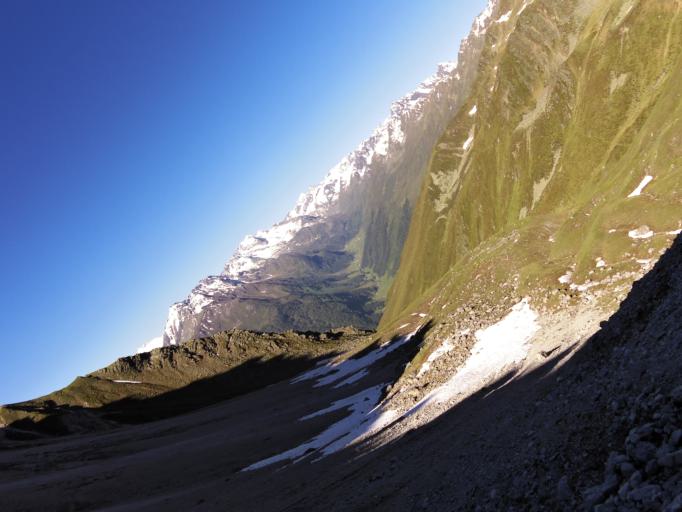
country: AT
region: Tyrol
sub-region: Politischer Bezirk Innsbruck Land
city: Neustift im Stubaital
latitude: 47.1374
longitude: 11.2759
